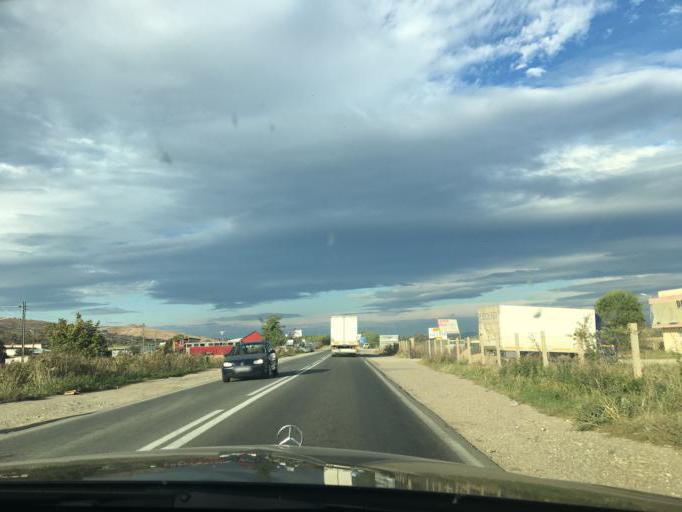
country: RO
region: Alba
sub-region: Municipiul Alba Iulia
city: Barabant
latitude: 46.0998
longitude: 23.6065
